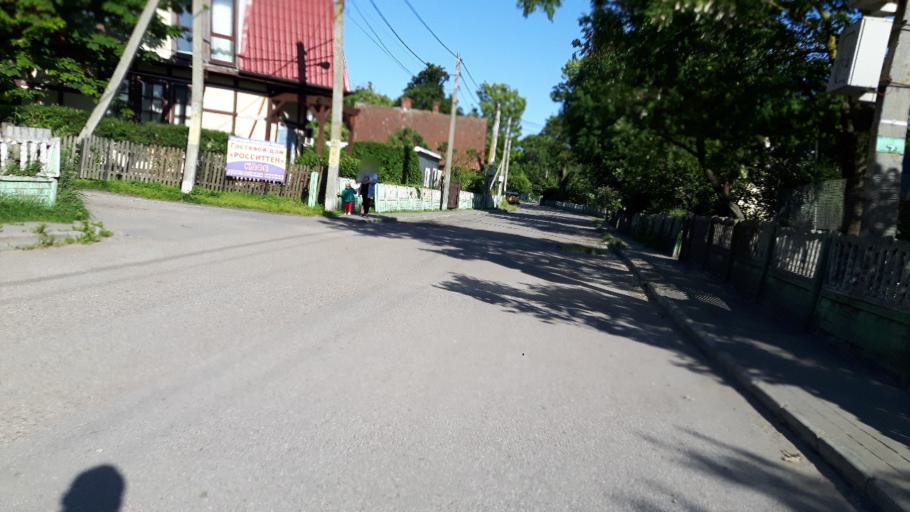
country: LT
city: Nida
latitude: 55.1540
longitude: 20.8537
